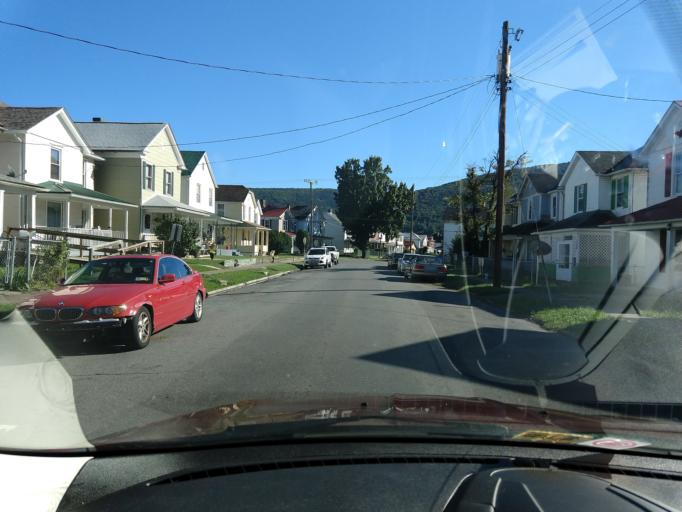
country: US
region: Virginia
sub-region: Alleghany County
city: Clifton Forge
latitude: 37.8185
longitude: -79.8280
